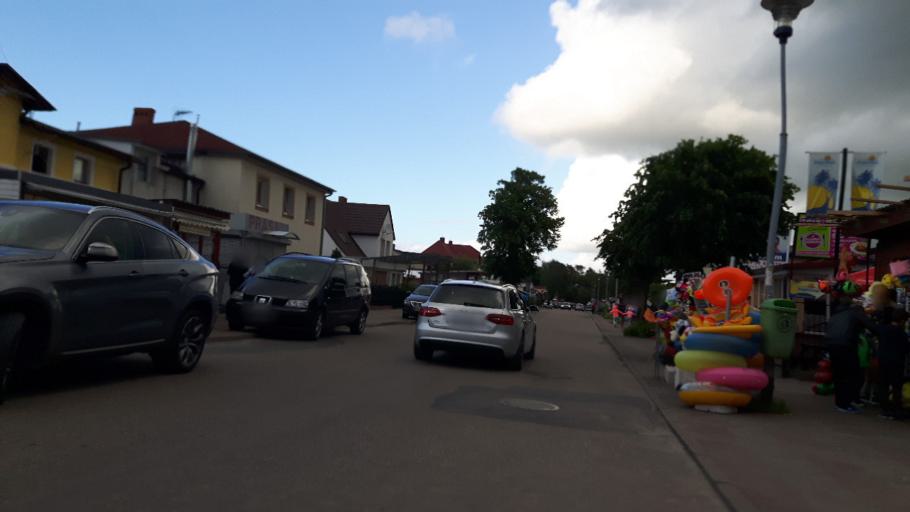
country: PL
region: West Pomeranian Voivodeship
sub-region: Powiat kolobrzeski
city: Ustronie Morskie
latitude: 54.2080
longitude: 15.7247
